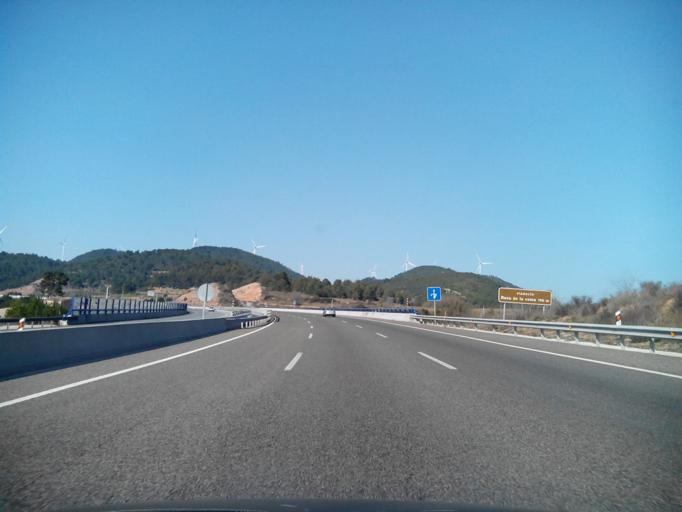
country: ES
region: Catalonia
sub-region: Provincia de Lleida
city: Sant Guim de Freixenet
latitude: 41.6304
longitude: 1.4741
